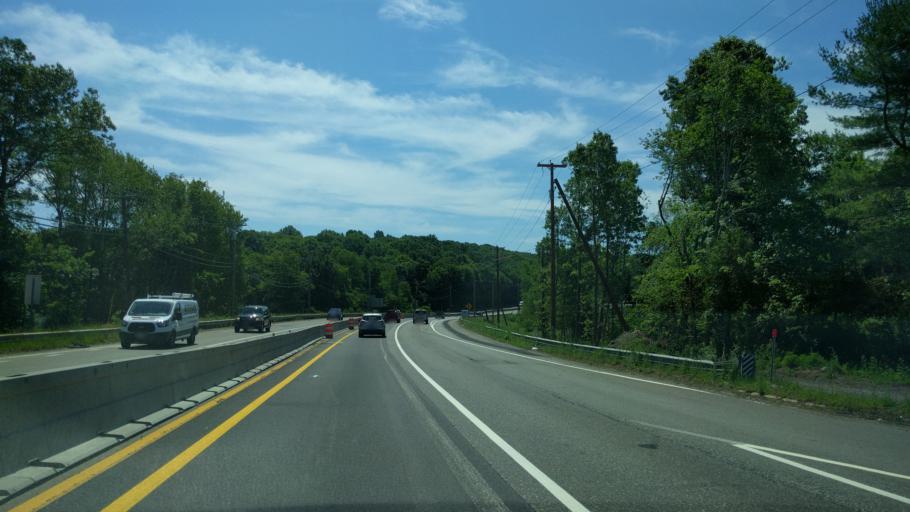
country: US
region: Massachusetts
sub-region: Worcester County
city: Millbury
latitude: 42.1865
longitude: -71.7651
